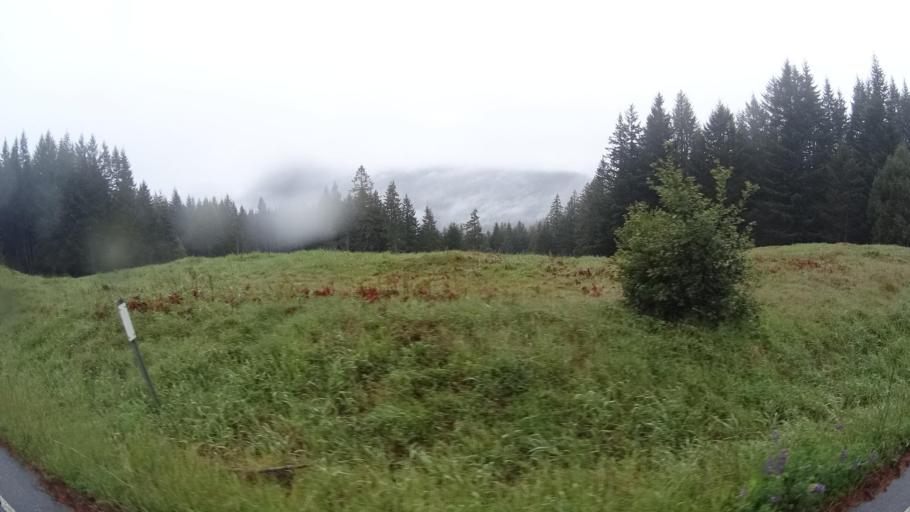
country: US
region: California
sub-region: Humboldt County
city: Westhaven-Moonstone
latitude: 41.2038
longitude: -123.9474
